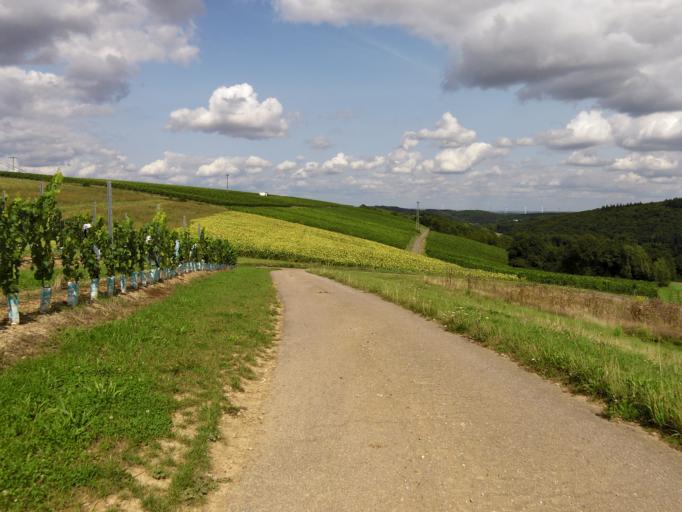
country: DE
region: Rheinland-Pfalz
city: Niederhausen an der Appel
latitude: 49.7625
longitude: 7.9013
